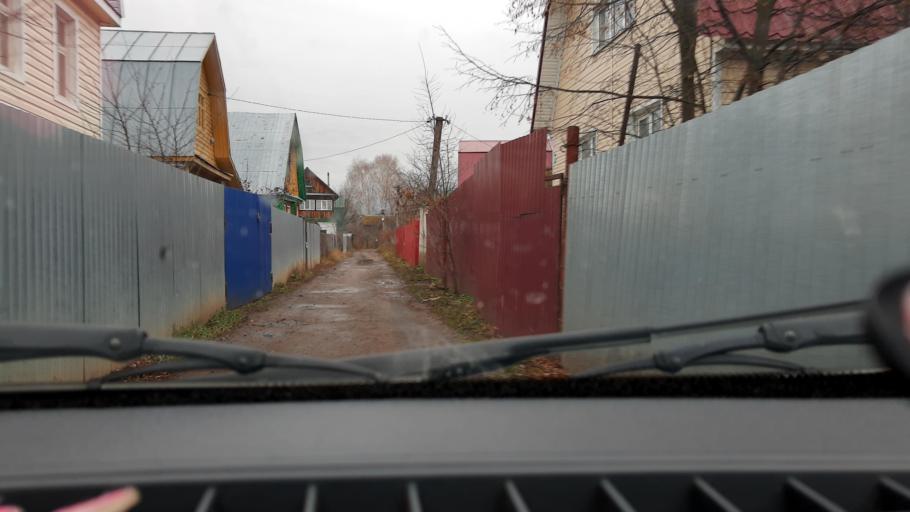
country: RU
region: Bashkortostan
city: Ufa
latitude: 54.6950
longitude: 55.8942
